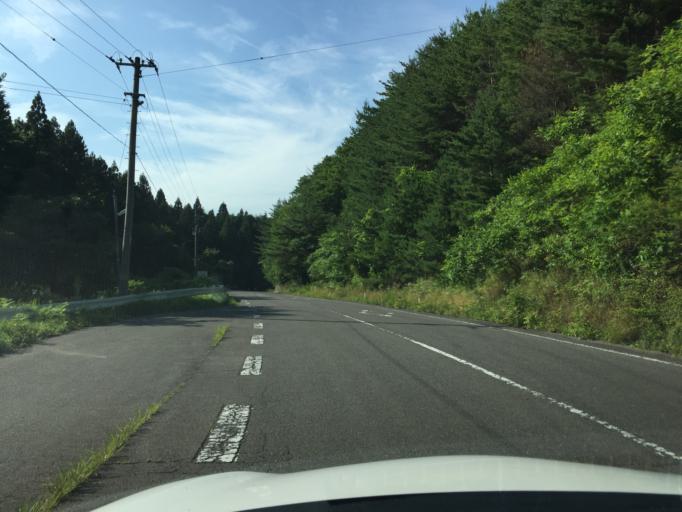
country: JP
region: Fukushima
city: Sukagawa
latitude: 37.2793
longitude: 140.5041
